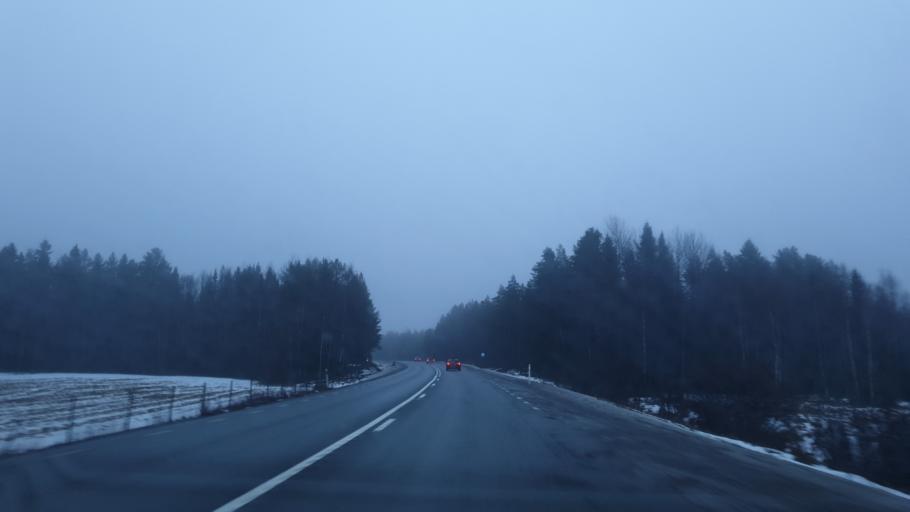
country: SE
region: Vaesterbotten
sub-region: Robertsfors Kommun
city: Robertsfors
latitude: 64.0215
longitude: 20.8389
